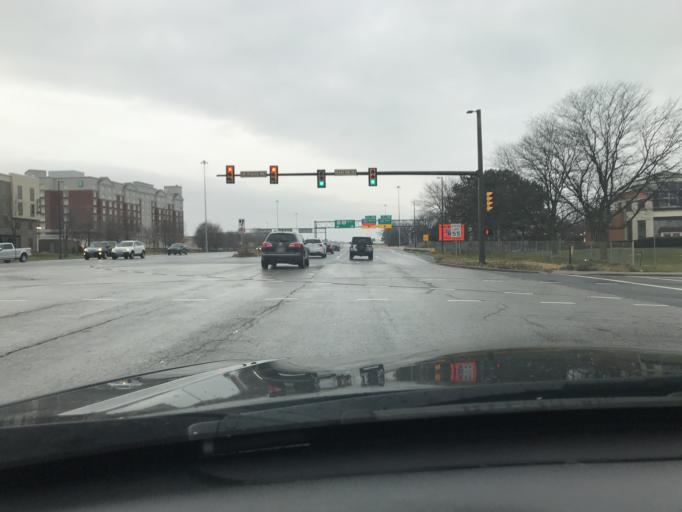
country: US
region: Ohio
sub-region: Franklin County
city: Dublin
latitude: 40.0993
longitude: -83.1244
